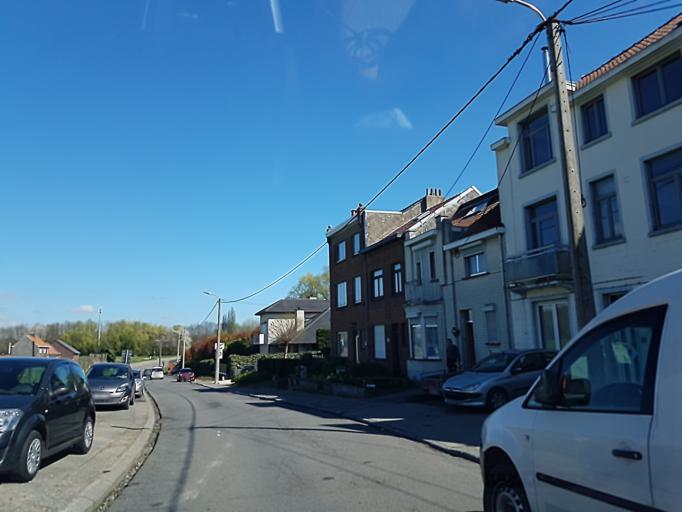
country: BE
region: Flanders
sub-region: Provincie Vlaams-Brabant
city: Dilbeek
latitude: 50.8481
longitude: 4.2732
